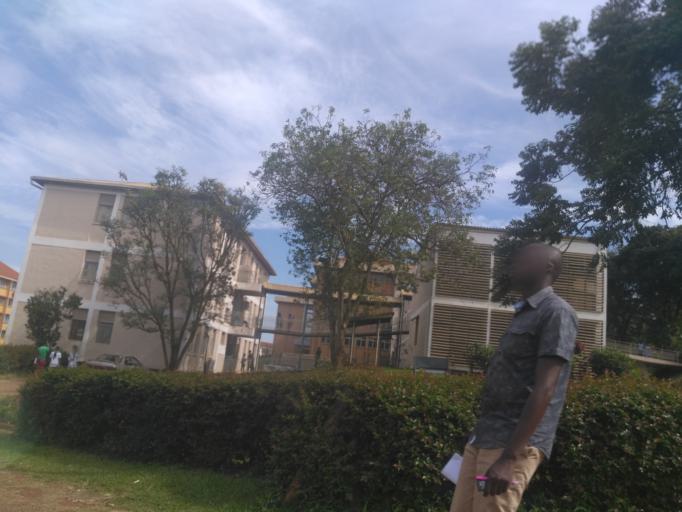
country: UG
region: Central Region
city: Kampala Central Division
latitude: 0.3335
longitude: 32.5684
